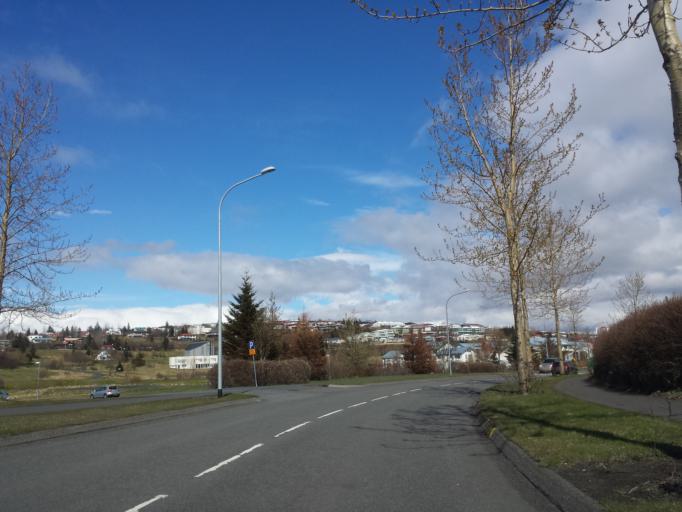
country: IS
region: Capital Region
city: Kopavogur
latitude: 64.1042
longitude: -21.8918
